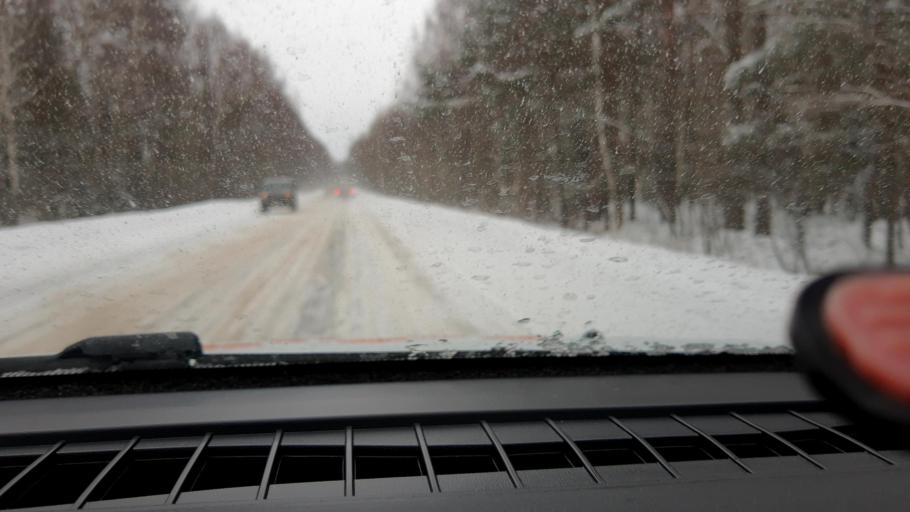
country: RU
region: Nizjnij Novgorod
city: Pamyat' Parizhskoy Kommuny
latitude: 56.2579
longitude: 44.4588
